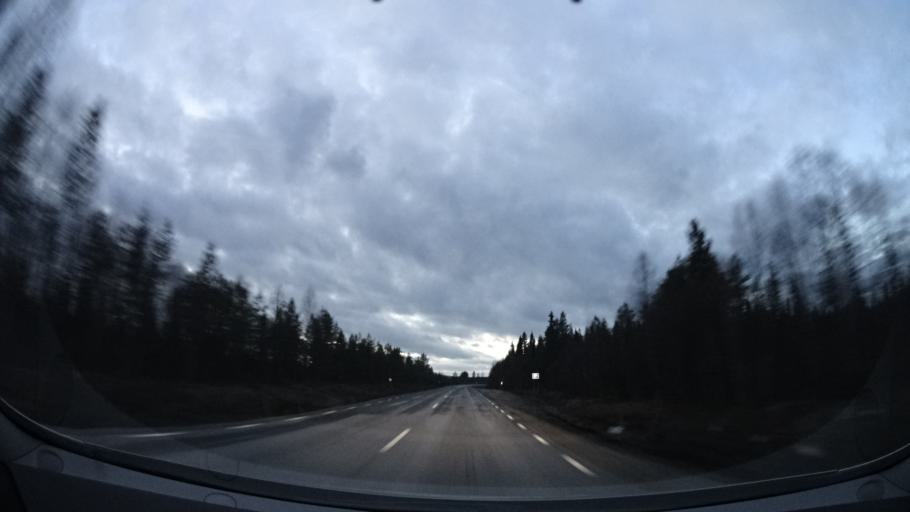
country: SE
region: Vaesterbotten
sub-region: Asele Kommun
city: Asele
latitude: 64.1836
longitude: 17.2168
